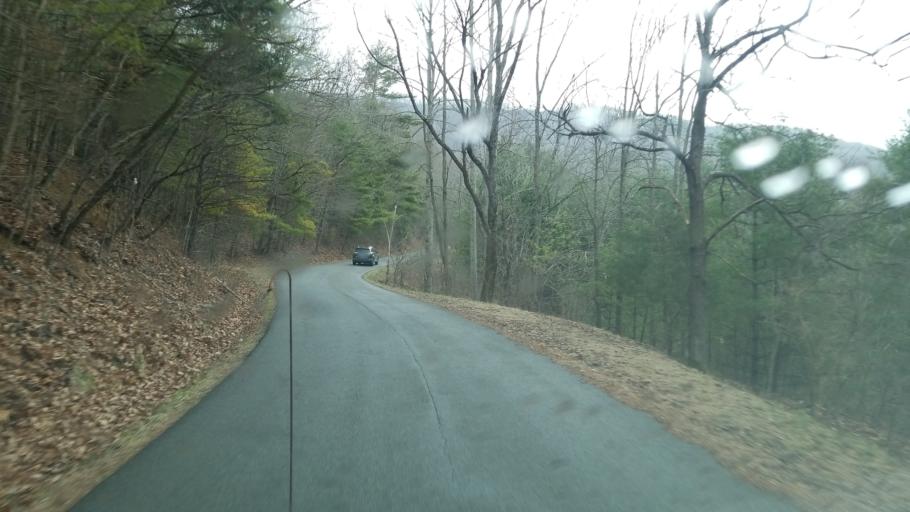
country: US
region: Virginia
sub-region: Giles County
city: Pearisburg
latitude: 37.2213
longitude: -80.7007
